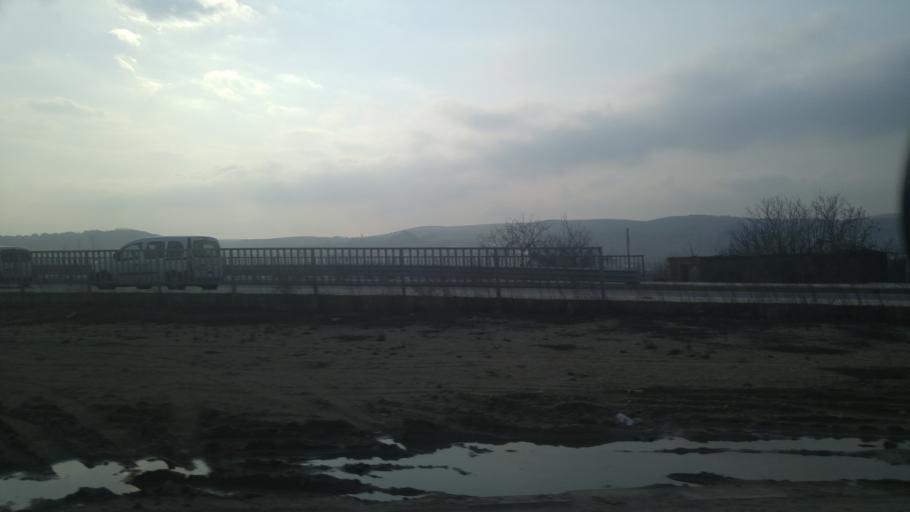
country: TR
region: Istanbul
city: Muratbey
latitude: 41.0888
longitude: 28.5143
